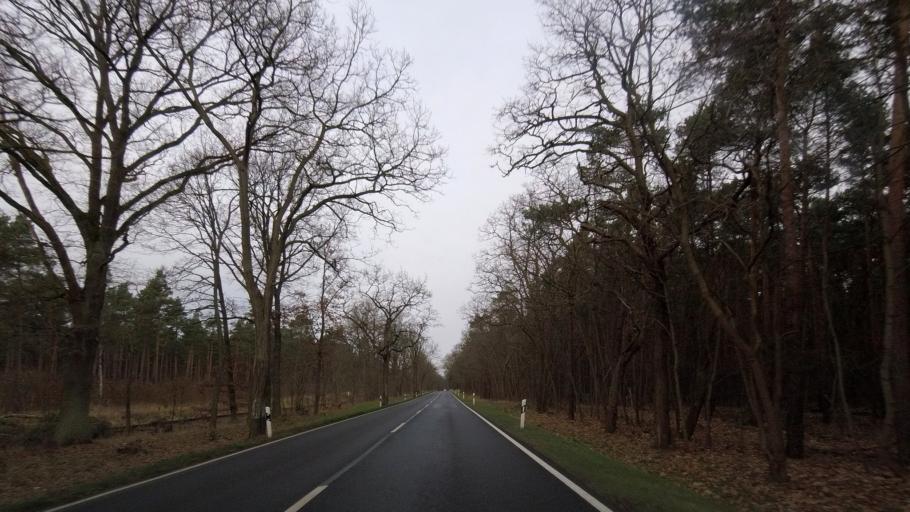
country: DE
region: Brandenburg
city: Treuenbrietzen
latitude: 52.0712
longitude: 12.8884
